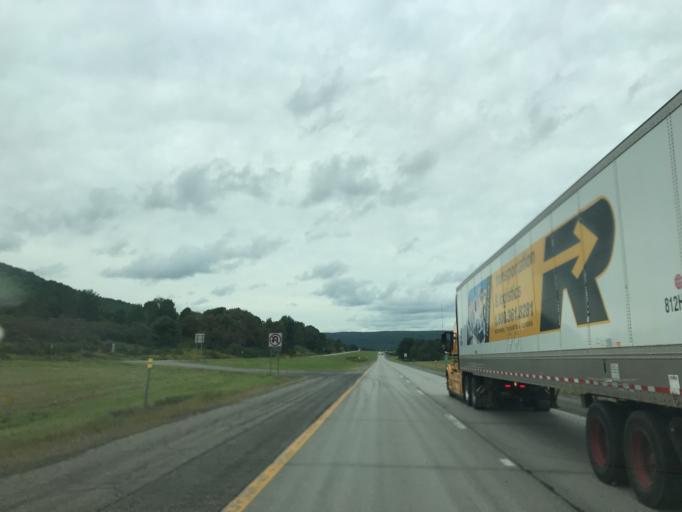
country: US
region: New York
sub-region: Otsego County
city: Oneonta
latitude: 42.4658
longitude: -75.0045
